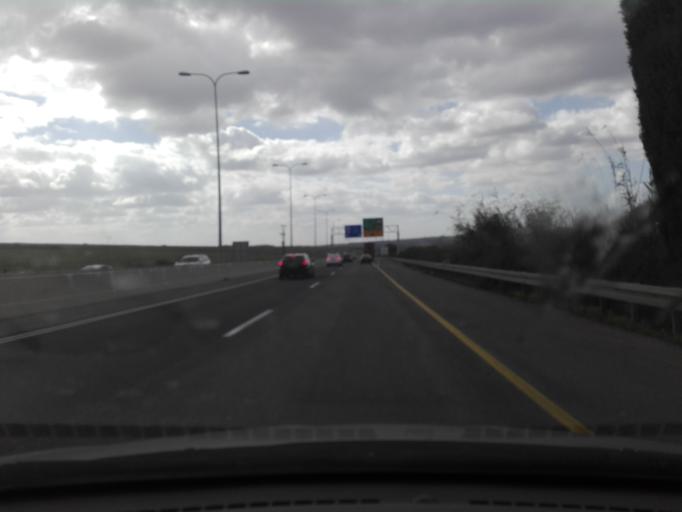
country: IL
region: Haifa
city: Daliyat el Karmil
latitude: 32.6236
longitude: 35.0585
